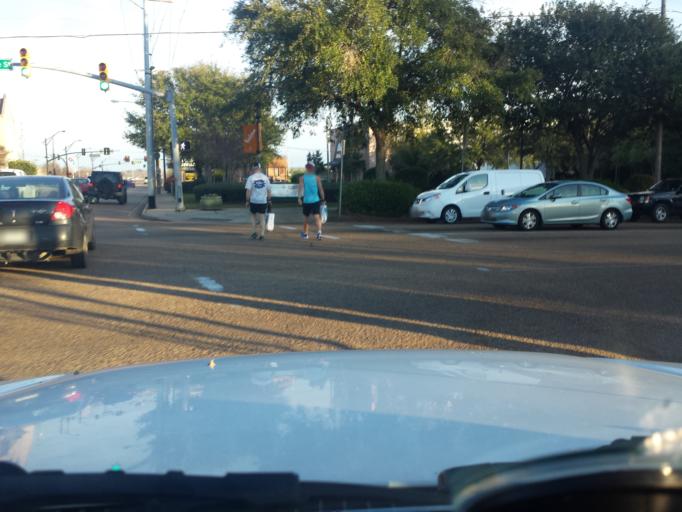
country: US
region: Mississippi
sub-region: Hinds County
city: Jackson
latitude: 32.3045
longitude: -90.1795
